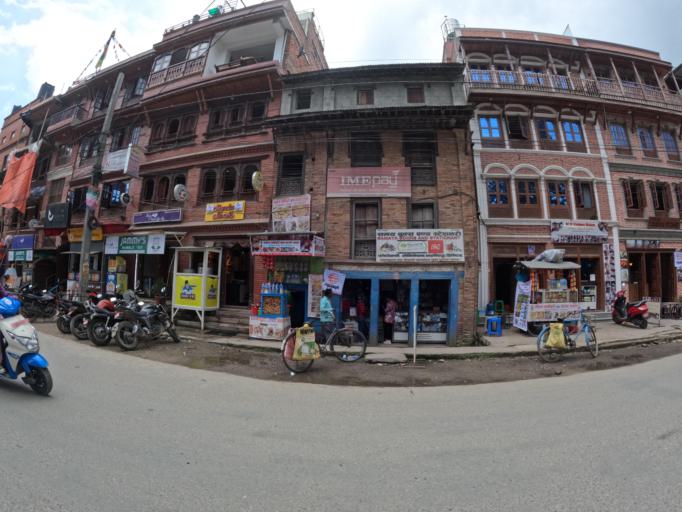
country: NP
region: Central Region
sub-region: Bagmati Zone
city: Bhaktapur
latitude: 27.6714
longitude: 85.4212
